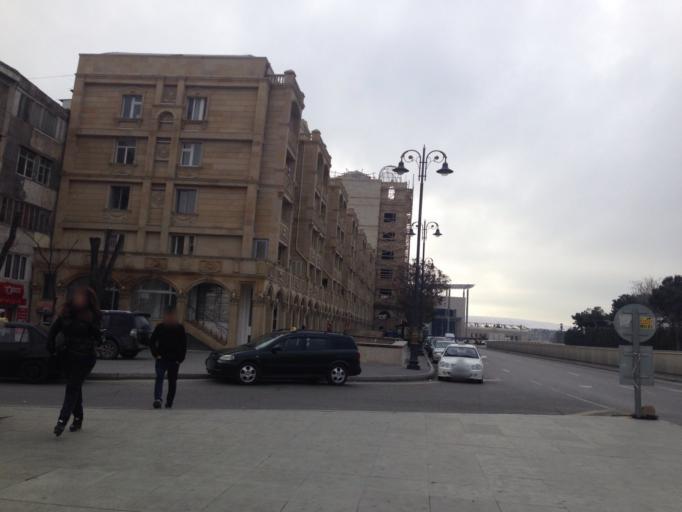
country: AZ
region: Baki
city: Baku
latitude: 40.4027
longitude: 49.8511
